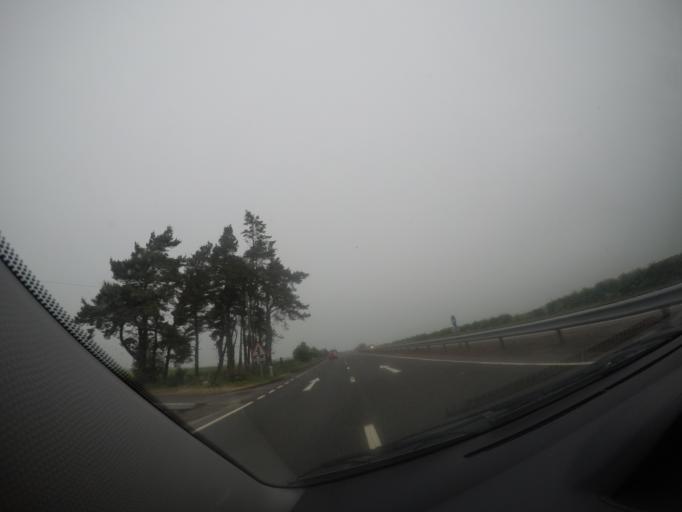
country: GB
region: Scotland
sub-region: Angus
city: Forfar
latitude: 56.5621
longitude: -2.9220
